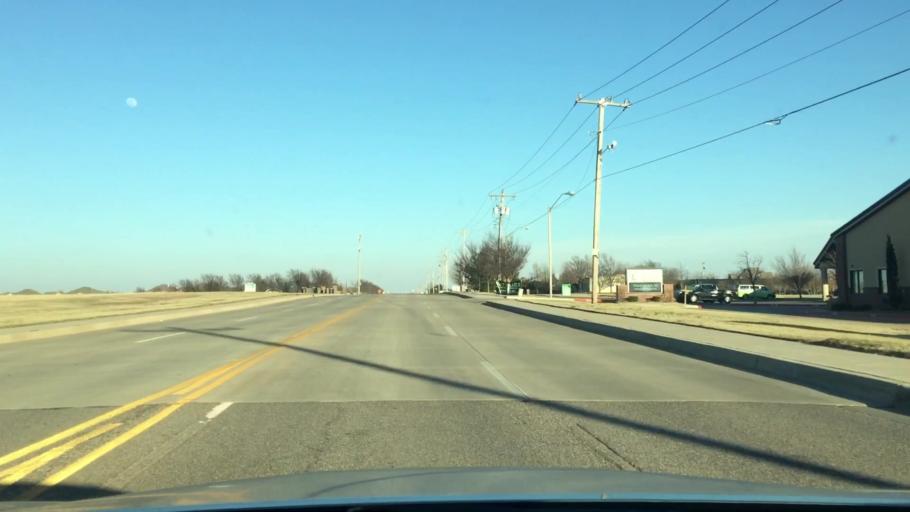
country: US
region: Oklahoma
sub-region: Oklahoma County
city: Edmond
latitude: 35.6531
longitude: -97.5659
